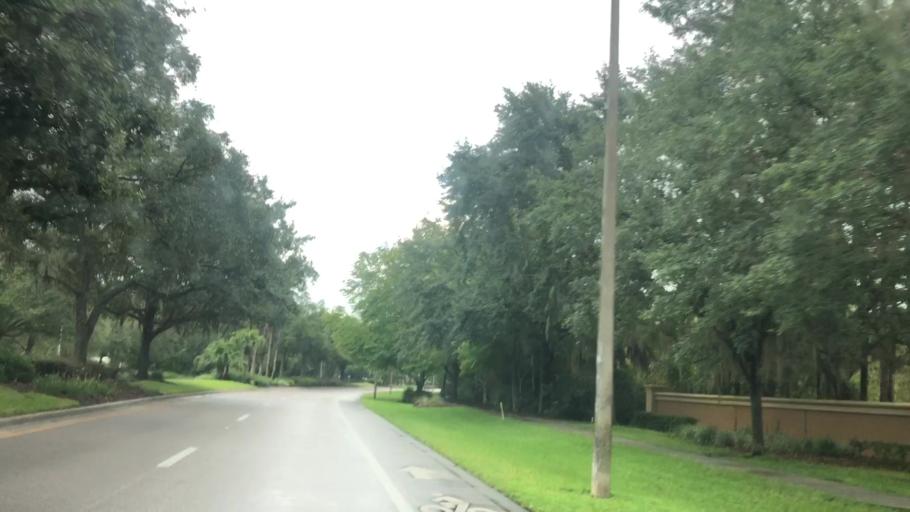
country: US
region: Florida
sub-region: Hillsborough County
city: Pebble Creek
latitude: 28.1167
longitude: -82.3872
